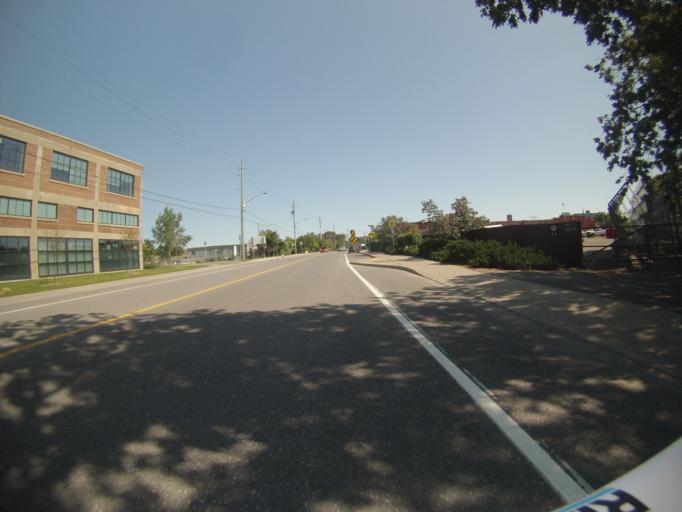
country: CA
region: Ontario
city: Ottawa
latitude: 45.4093
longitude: -75.7280
